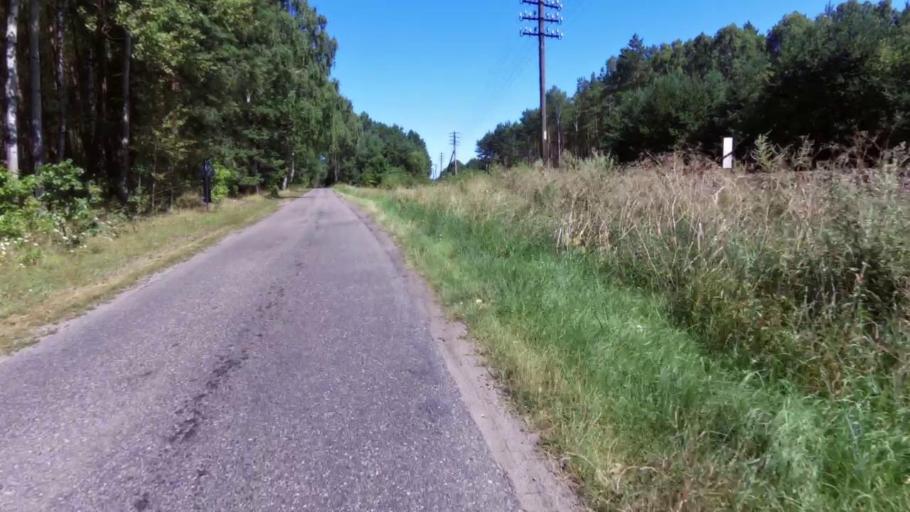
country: PL
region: West Pomeranian Voivodeship
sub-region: Powiat szczecinecki
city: Lubowo
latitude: 53.5731
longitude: 16.3654
